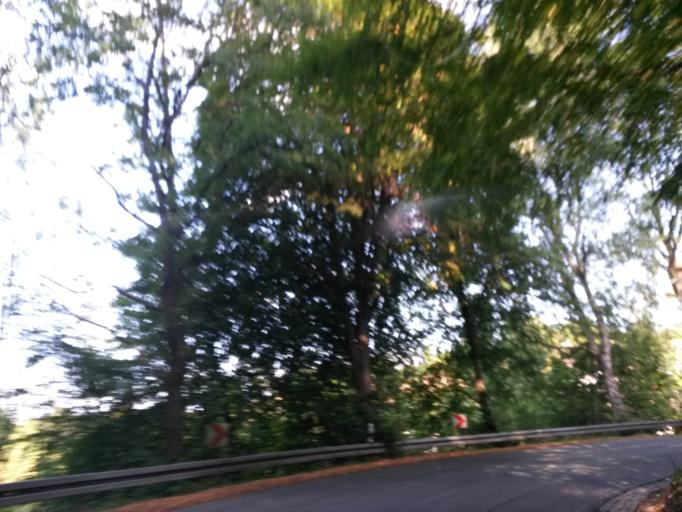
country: DE
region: North Rhine-Westphalia
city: Wiehl
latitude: 50.9757
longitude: 7.5177
